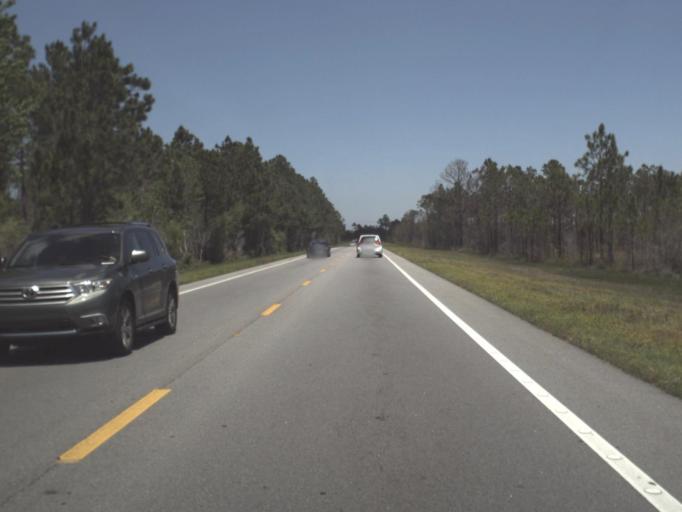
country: US
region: Florida
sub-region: Escambia County
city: Myrtle Grove
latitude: 30.3867
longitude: -87.3470
